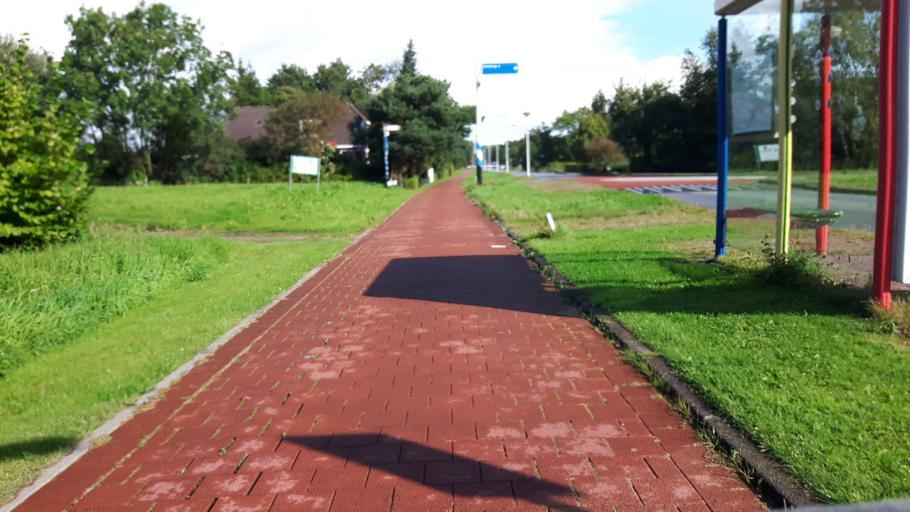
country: NL
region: Friesland
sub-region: Gemeente Smallingerland
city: Drachten
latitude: 53.0883
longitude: 6.0996
